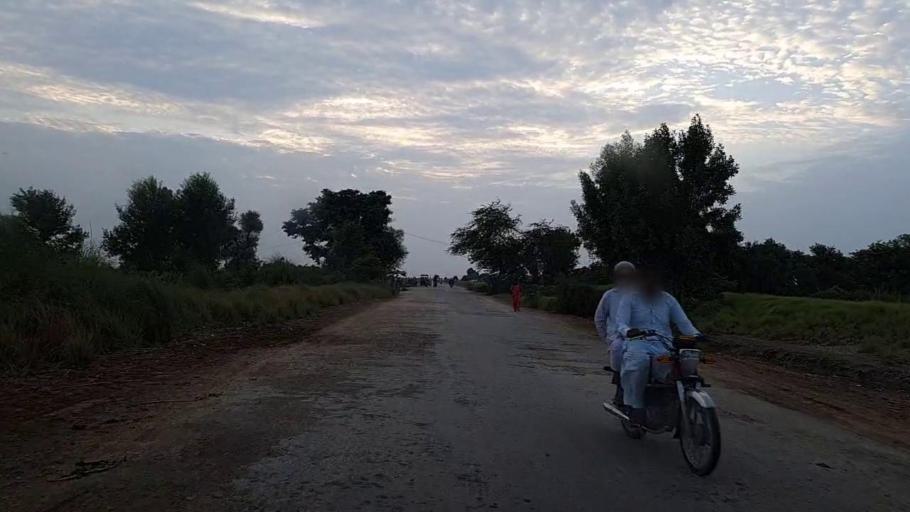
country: PK
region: Sindh
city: Naushahro Firoz
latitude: 26.8212
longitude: 68.1666
